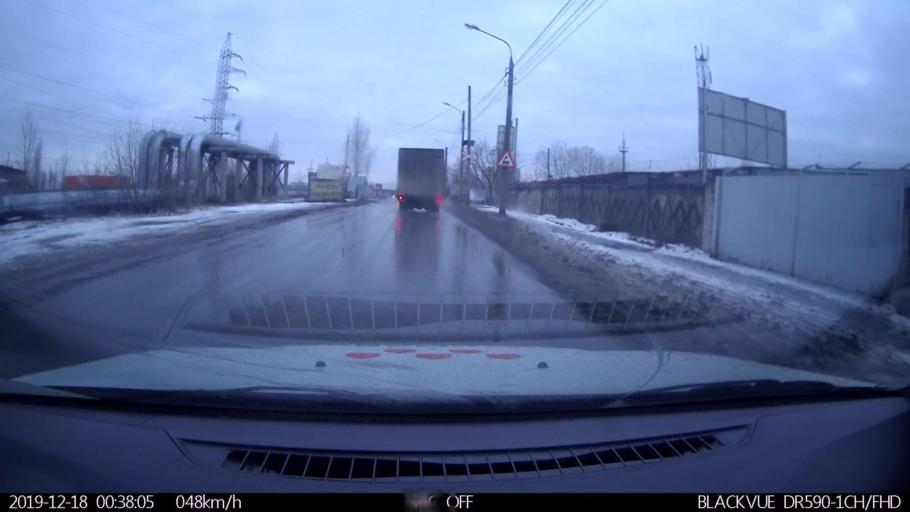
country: RU
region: Nizjnij Novgorod
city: Neklyudovo
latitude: 56.3482
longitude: 43.8923
